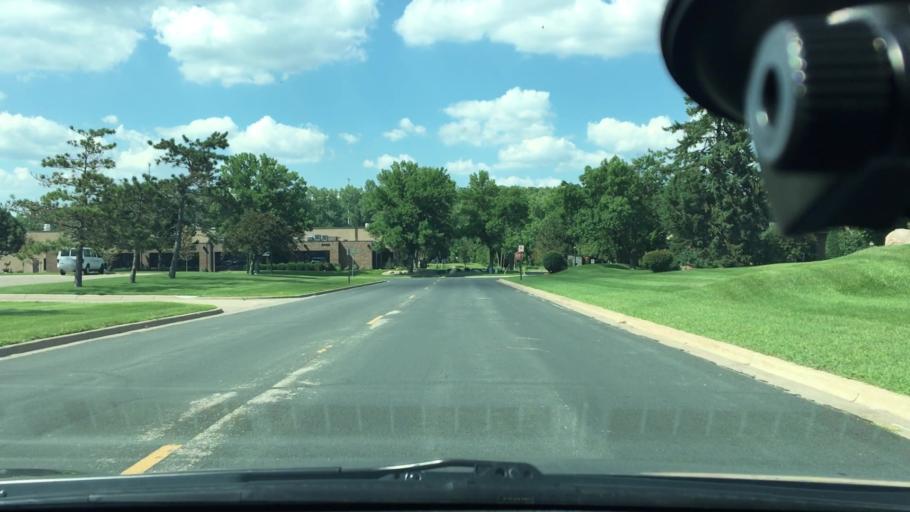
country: US
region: Minnesota
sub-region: Hennepin County
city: Golden Valley
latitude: 44.9882
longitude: -93.3928
